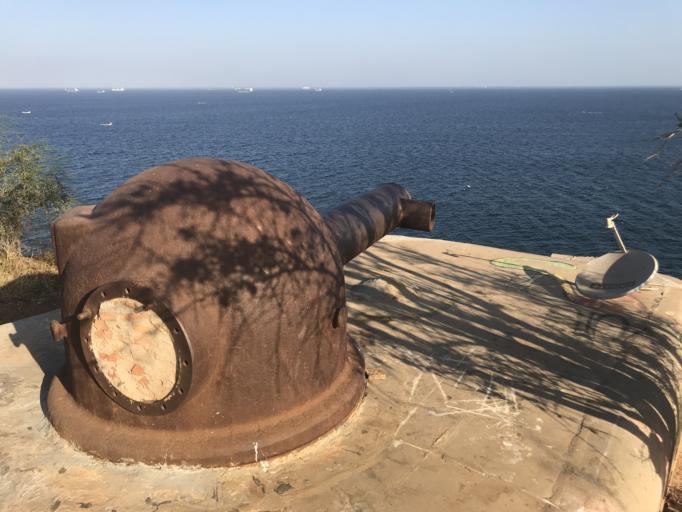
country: SN
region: Dakar
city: Dakar
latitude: 14.6640
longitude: -17.3977
